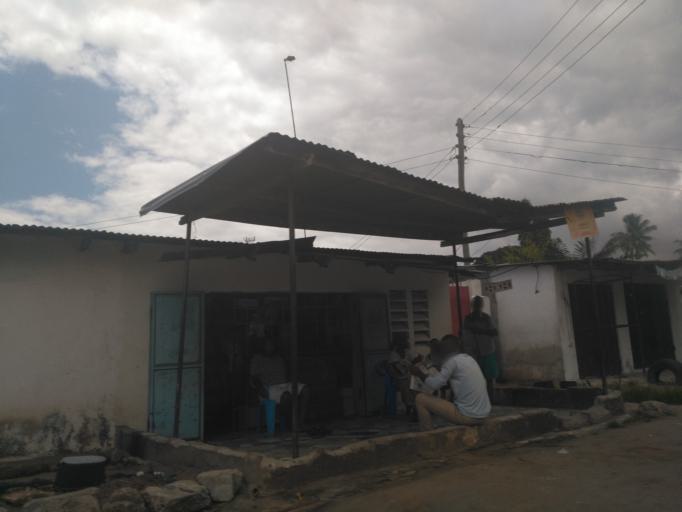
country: TZ
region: Dar es Salaam
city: Magomeni
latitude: -6.7928
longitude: 39.2705
